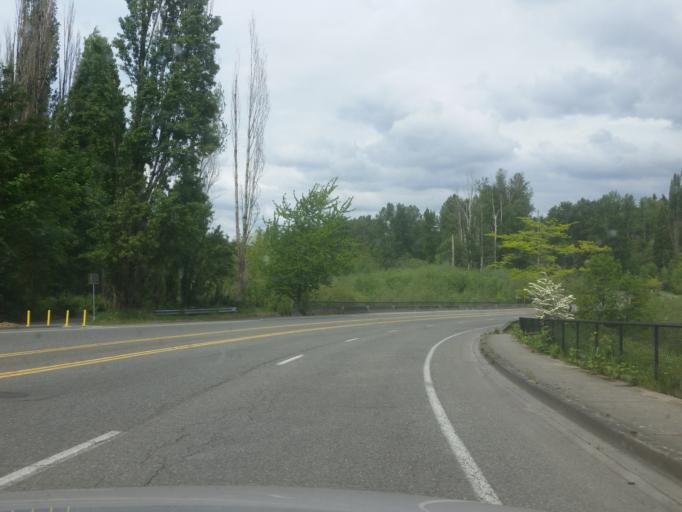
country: US
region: Washington
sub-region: King County
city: Kirkland
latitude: 47.6960
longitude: -122.2100
